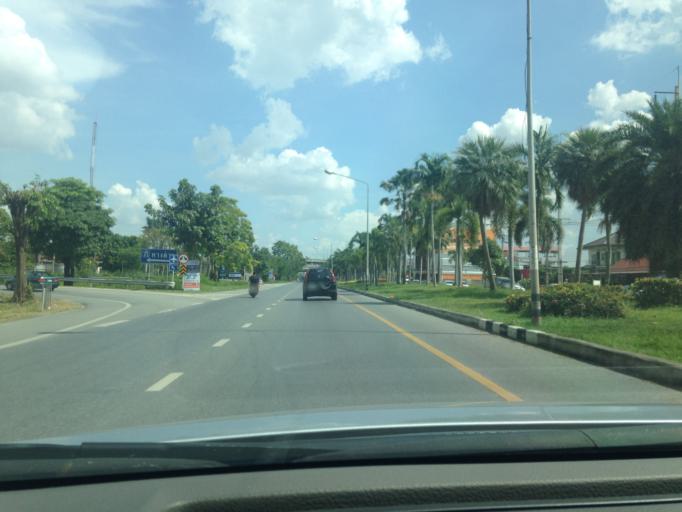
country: TH
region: Phra Nakhon Si Ayutthaya
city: Ban Bang Kadi Pathum Thani
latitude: 14.0051
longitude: 100.5648
